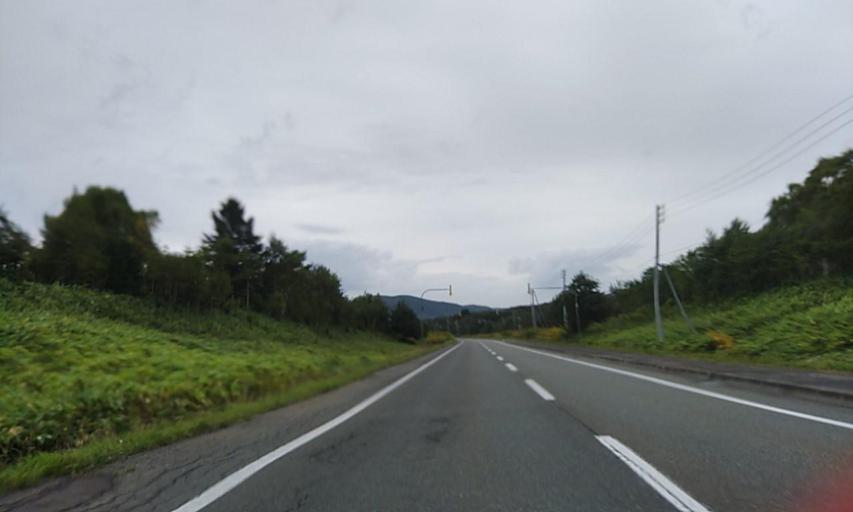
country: JP
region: Hokkaido
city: Nayoro
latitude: 45.0485
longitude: 142.4988
